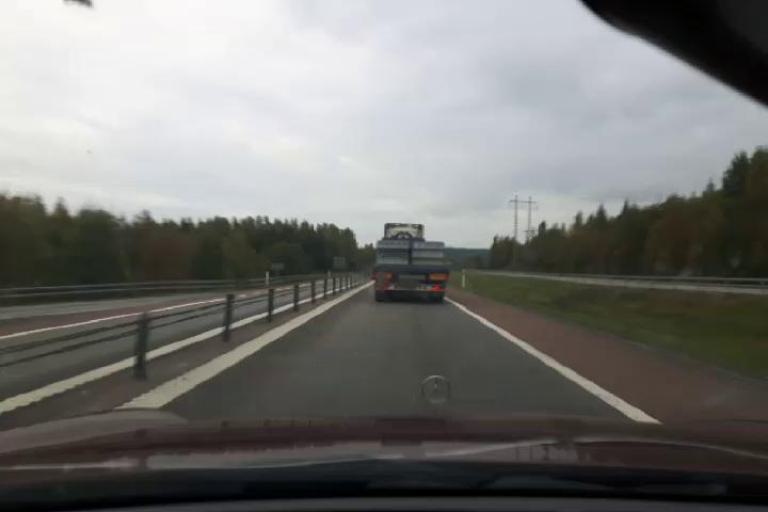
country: SE
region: Vaesternorrland
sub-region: Haernoesands Kommun
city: Haernoesand
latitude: 62.7765
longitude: 17.9191
